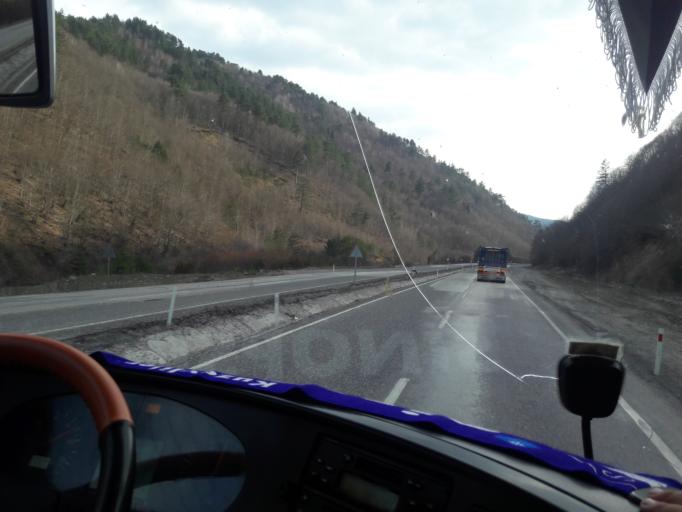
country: TR
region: Kastamonu
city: Kuzyaka
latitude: 41.1343
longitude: 33.7754
